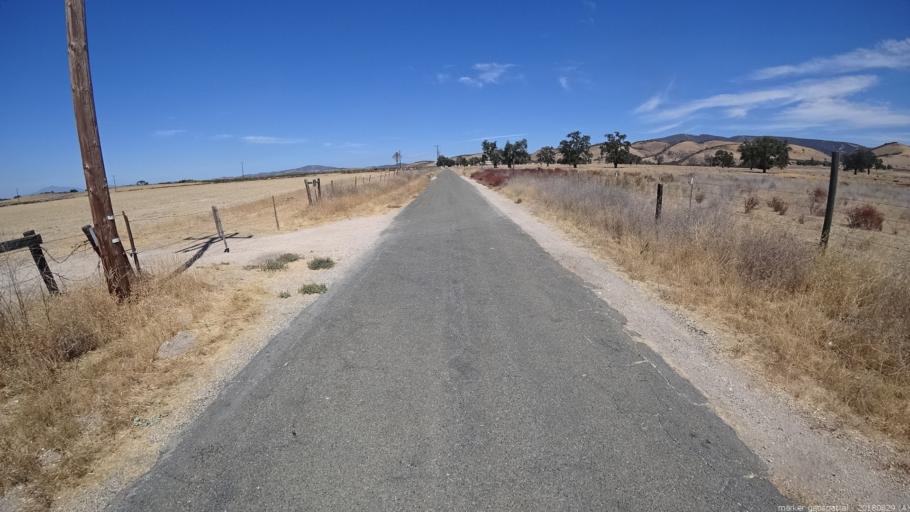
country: US
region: California
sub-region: San Luis Obispo County
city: Lake Nacimiento
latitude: 35.9097
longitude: -121.0380
